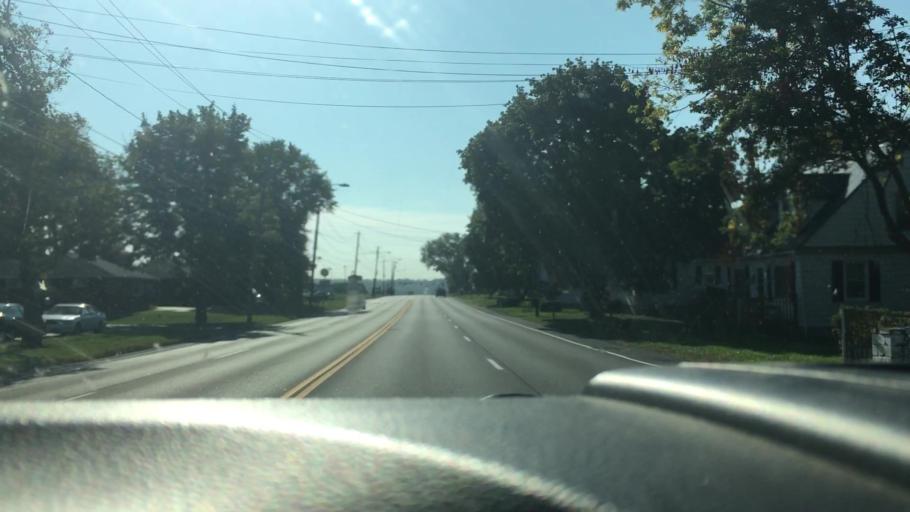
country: US
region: New York
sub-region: Onondaga County
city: Galeville
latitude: 43.0947
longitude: -76.1750
